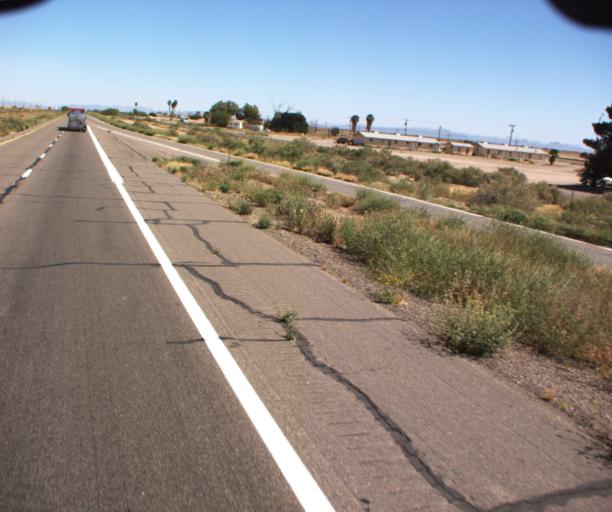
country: US
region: Arizona
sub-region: Maricopa County
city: Gila Bend
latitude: 32.9221
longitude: -112.8846
